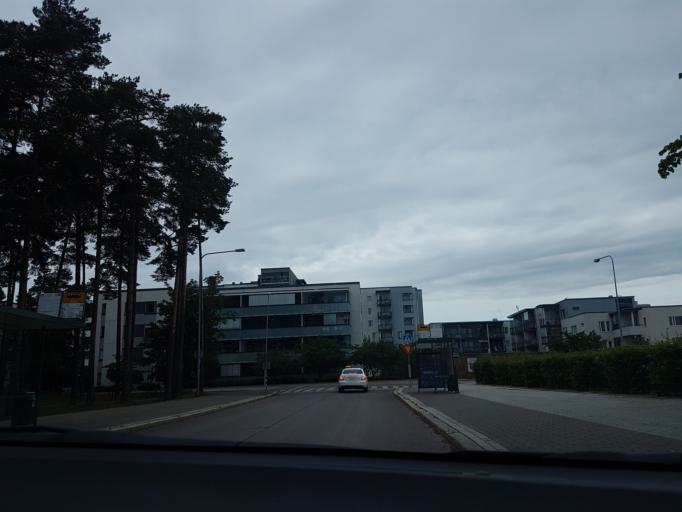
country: FI
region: Uusimaa
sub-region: Helsinki
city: Vantaa
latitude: 60.2091
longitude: 25.1428
